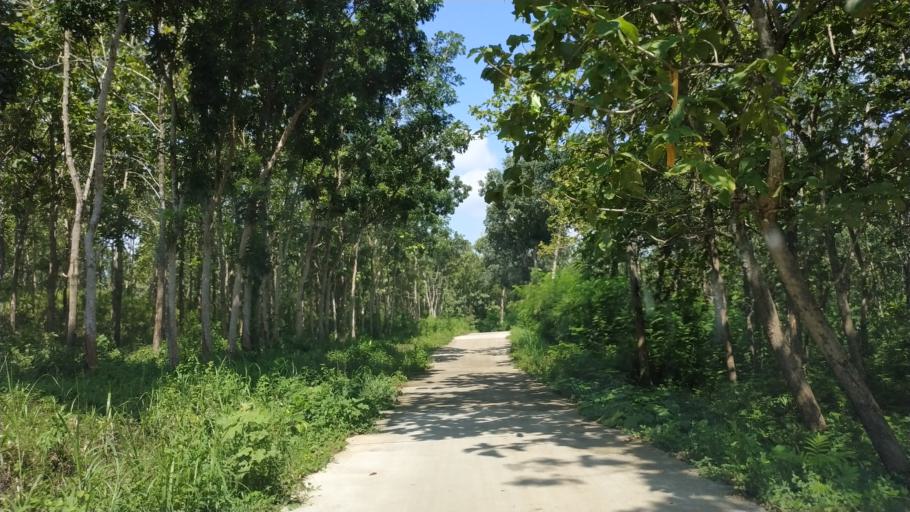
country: ID
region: Central Java
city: Guyangan
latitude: -7.0012
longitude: 111.0866
